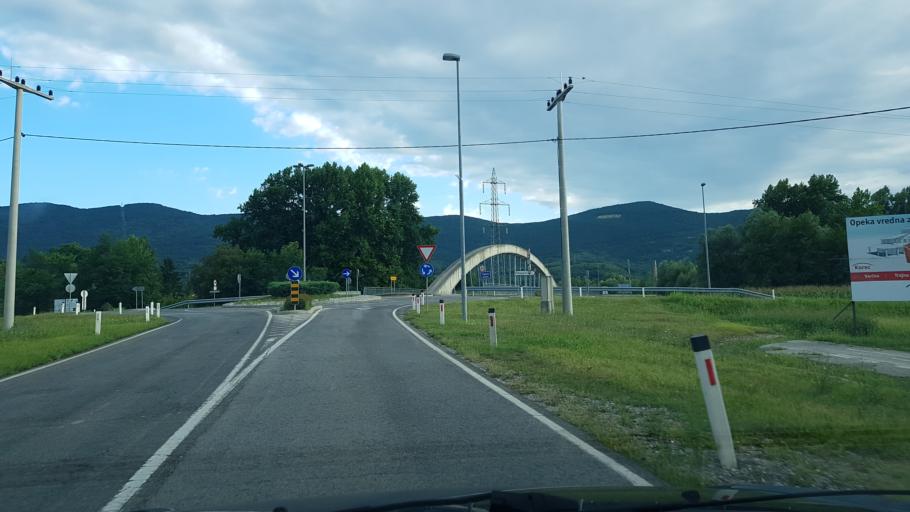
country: SI
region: Rence-Vogrsko
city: Rence
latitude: 45.8928
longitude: 13.6666
